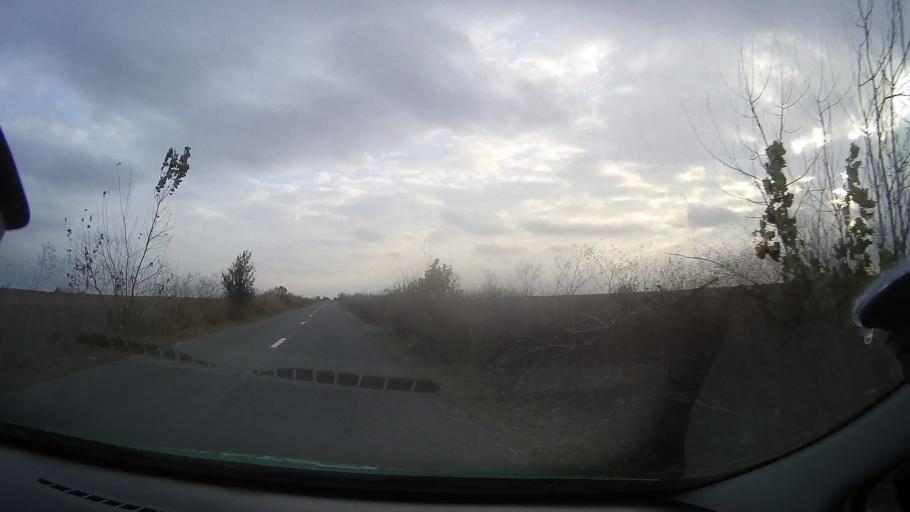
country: RO
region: Constanta
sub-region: Comuna Pestera
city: Pestera
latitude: 44.1418
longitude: 28.1167
